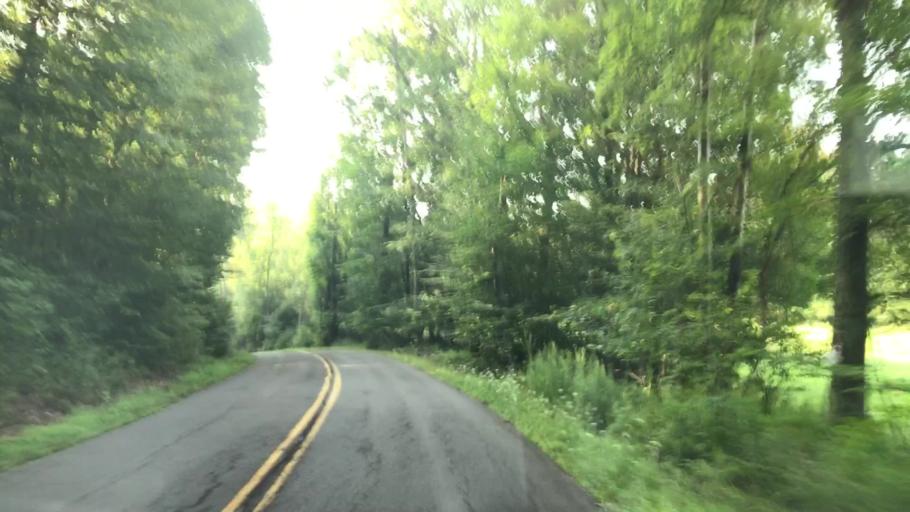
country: US
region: Pennsylvania
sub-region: Wyoming County
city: Factoryville
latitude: 41.6124
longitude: -75.7405
